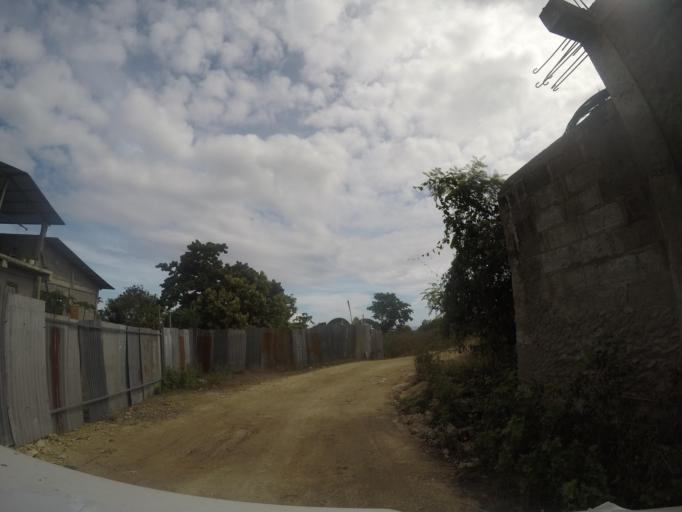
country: TL
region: Baucau
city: Baucau
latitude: -8.4693
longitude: 126.4567
